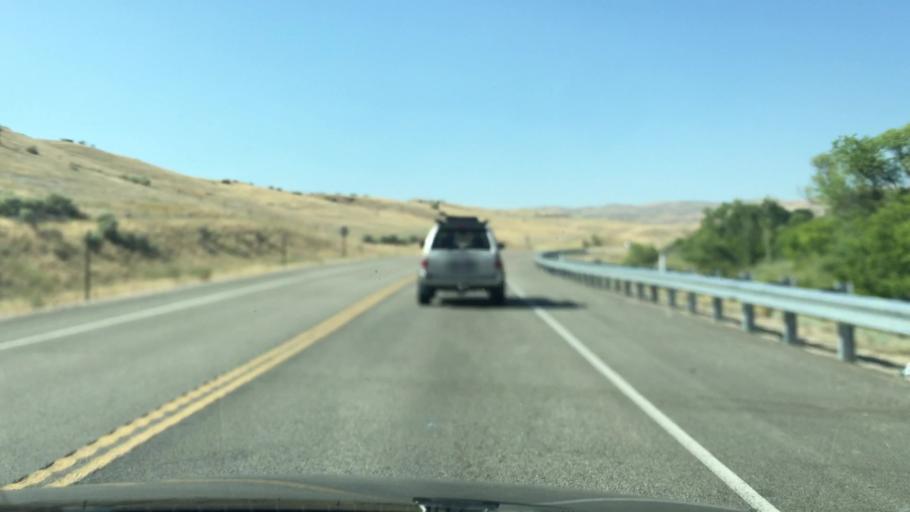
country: US
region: Idaho
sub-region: Ada County
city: Eagle
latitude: 43.7674
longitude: -116.2661
